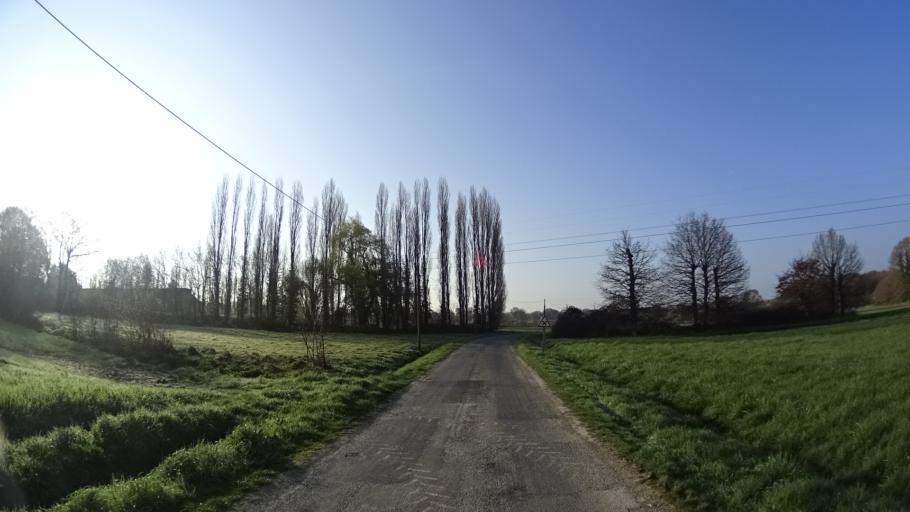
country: FR
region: Brittany
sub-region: Departement d'Ille-et-Vilaine
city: Geveze
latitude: 48.1956
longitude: -1.7764
